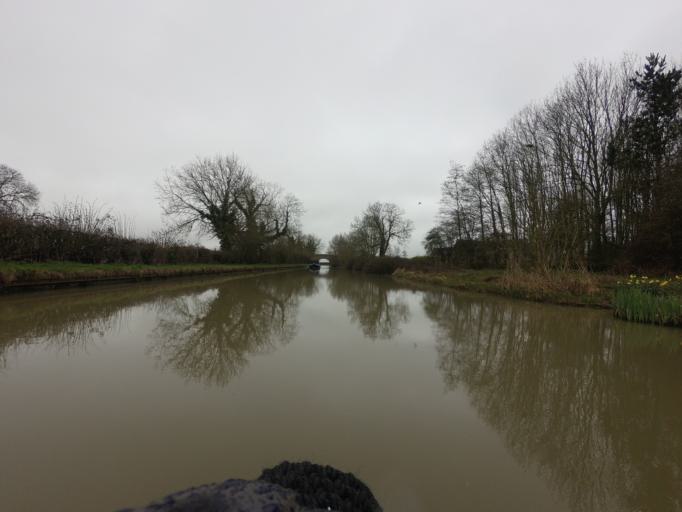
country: GB
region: England
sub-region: Milton Keynes
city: Castlethorpe
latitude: 52.0946
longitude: -0.8619
